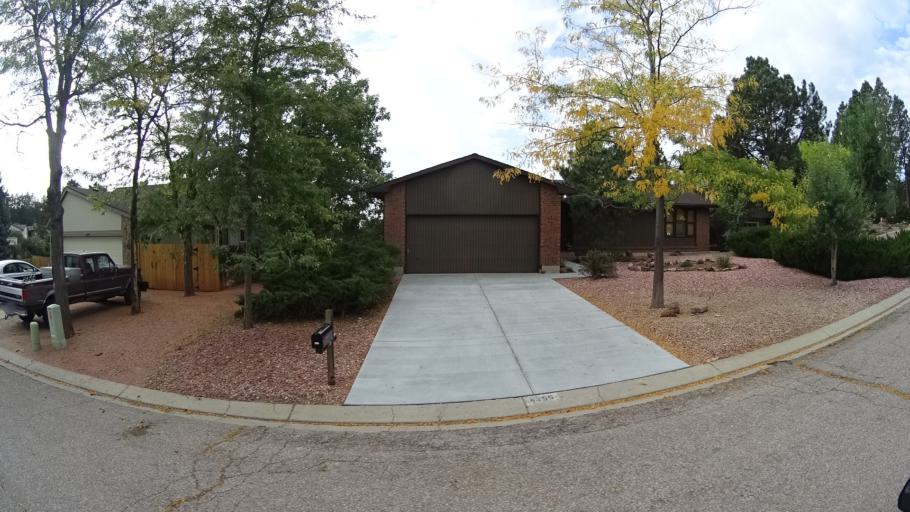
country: US
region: Colorado
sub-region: El Paso County
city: Cimarron Hills
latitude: 38.8682
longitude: -104.7484
